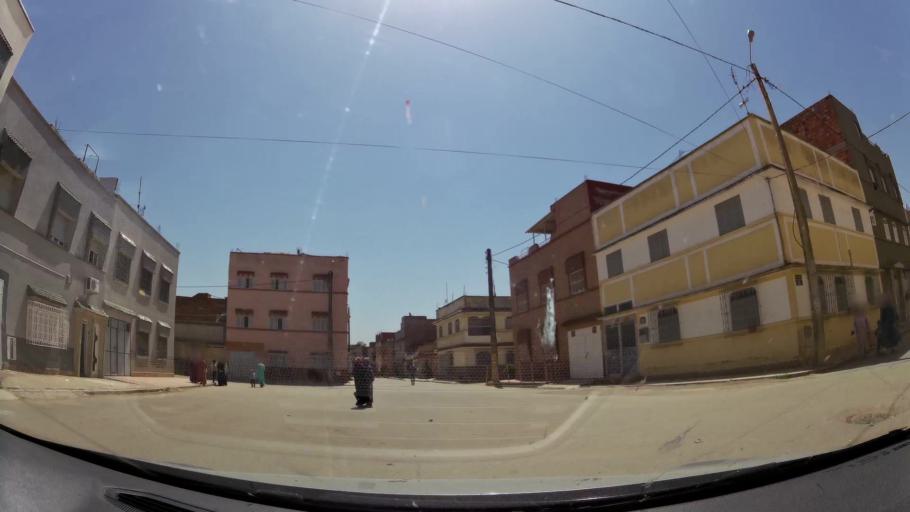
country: MA
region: Rabat-Sale-Zemmour-Zaer
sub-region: Khemisset
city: Khemisset
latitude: 33.8115
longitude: -6.0705
